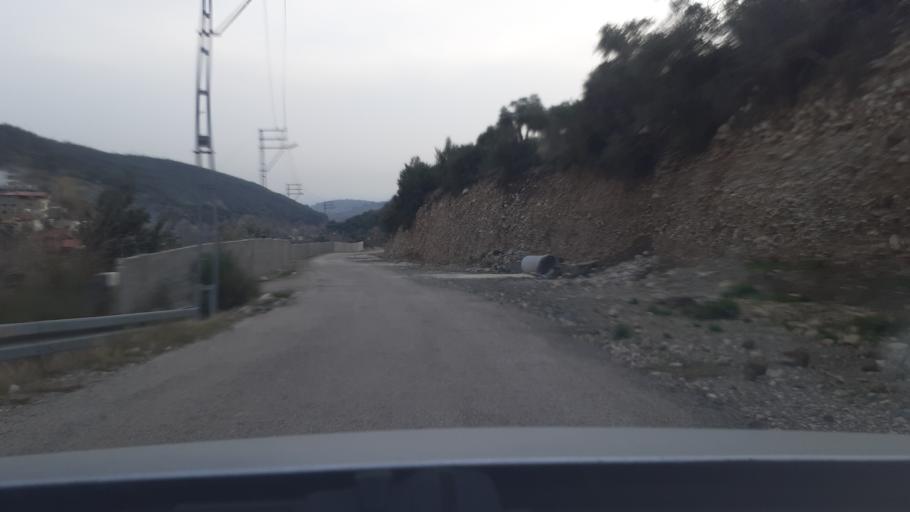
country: TR
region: Hatay
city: Kirikhan
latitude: 36.5297
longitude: 36.3166
